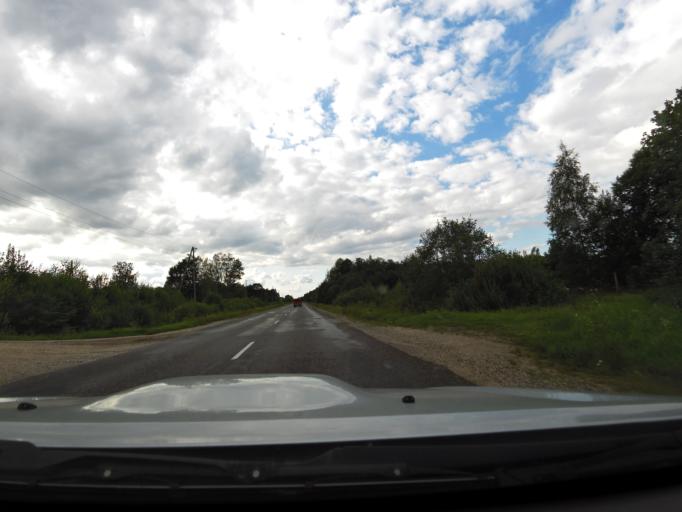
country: LV
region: Akniste
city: Akniste
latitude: 55.9931
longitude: 25.9730
